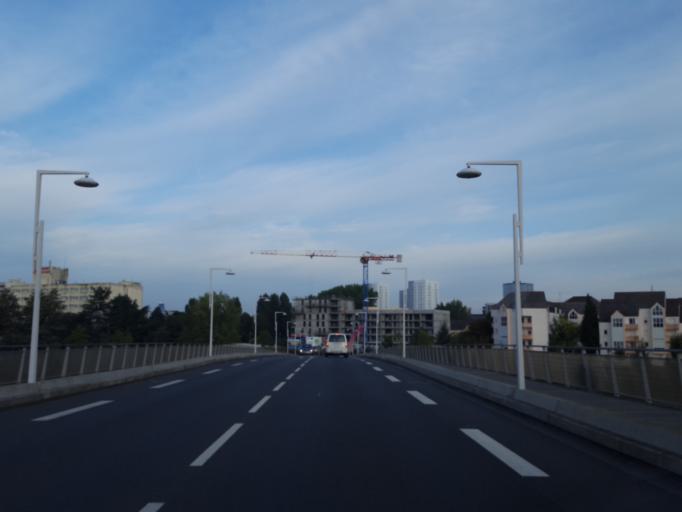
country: FR
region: Pays de la Loire
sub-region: Departement de la Loire-Atlantique
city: Saint-Sebastien-sur-Loire
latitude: 47.2059
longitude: -1.5251
